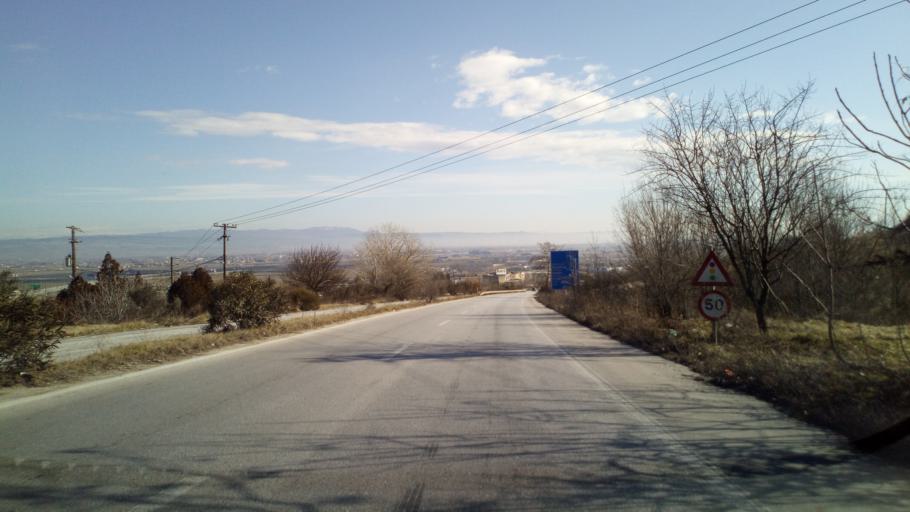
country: GR
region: Central Macedonia
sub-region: Nomos Thessalonikis
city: Lagyna
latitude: 40.7290
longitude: 22.9925
